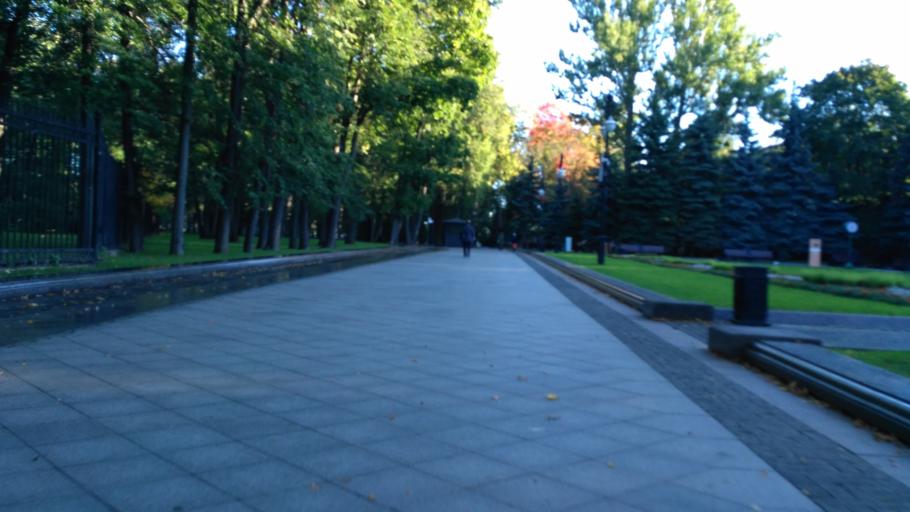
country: RU
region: Moscow
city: Ostankinskiy
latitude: 55.8260
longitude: 37.6171
